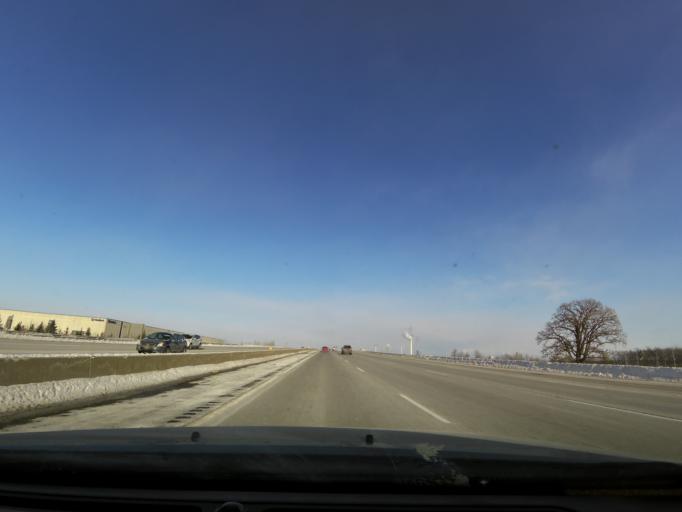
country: CA
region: Ontario
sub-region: Halton
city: Milton
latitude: 43.5302
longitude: -79.9003
